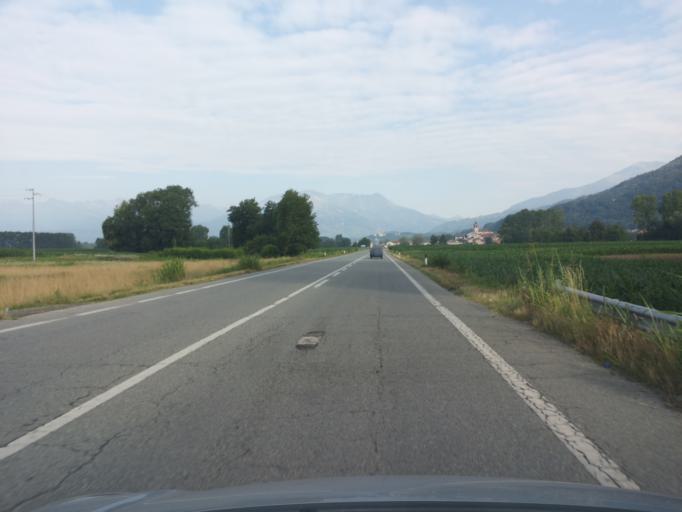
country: IT
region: Piedmont
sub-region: Provincia di Torino
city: Palazzo Canavese
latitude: 45.4509
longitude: 7.9879
